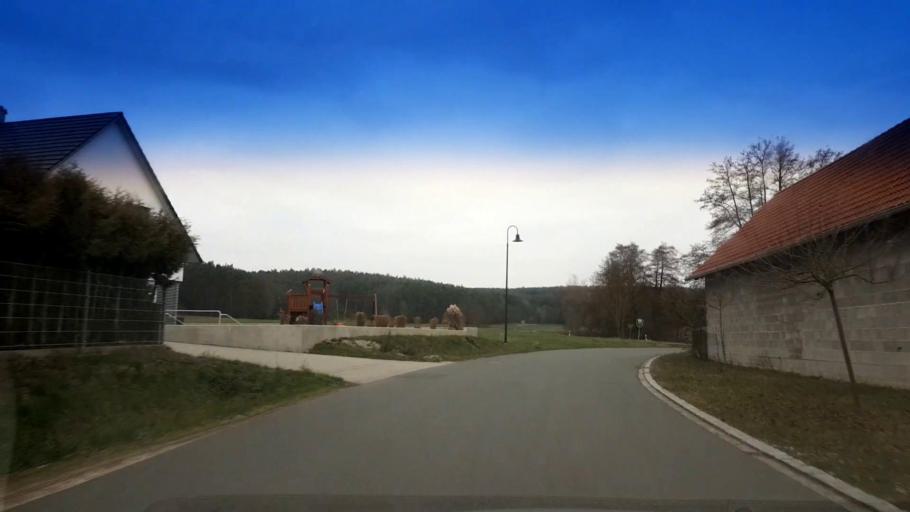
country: DE
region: Bavaria
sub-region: Upper Franconia
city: Pettstadt
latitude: 49.7765
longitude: 10.9150
